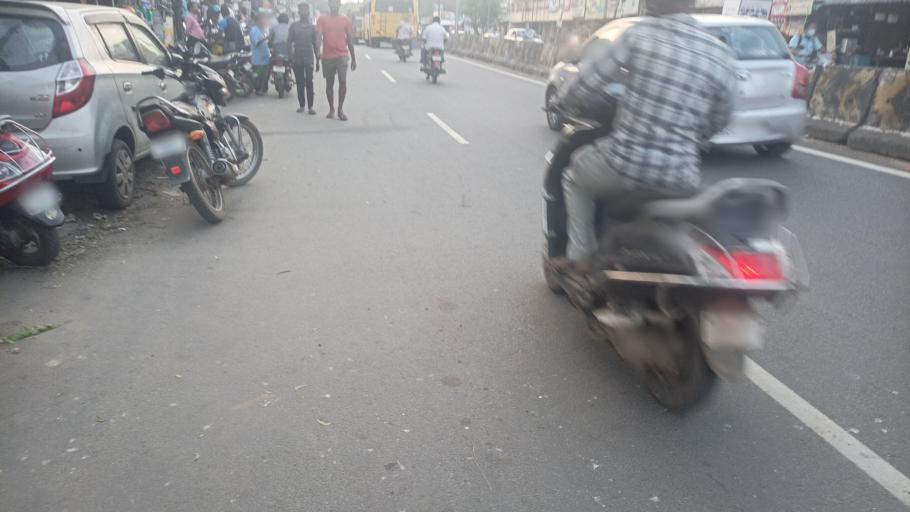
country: IN
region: Tamil Nadu
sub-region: Salem
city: Salem
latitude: 11.6739
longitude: 78.1231
